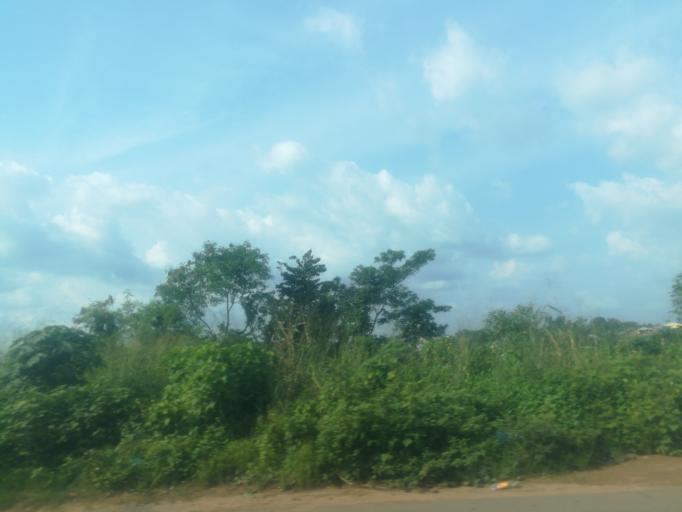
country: NG
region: Oyo
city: Ido
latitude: 7.3958
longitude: 3.7834
